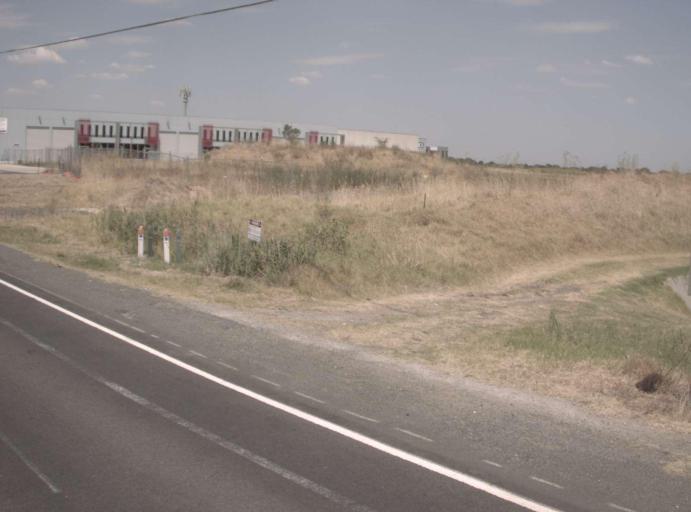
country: AU
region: Victoria
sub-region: Kingston
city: Aspendale Gardens
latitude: -38.0086
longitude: 145.1153
